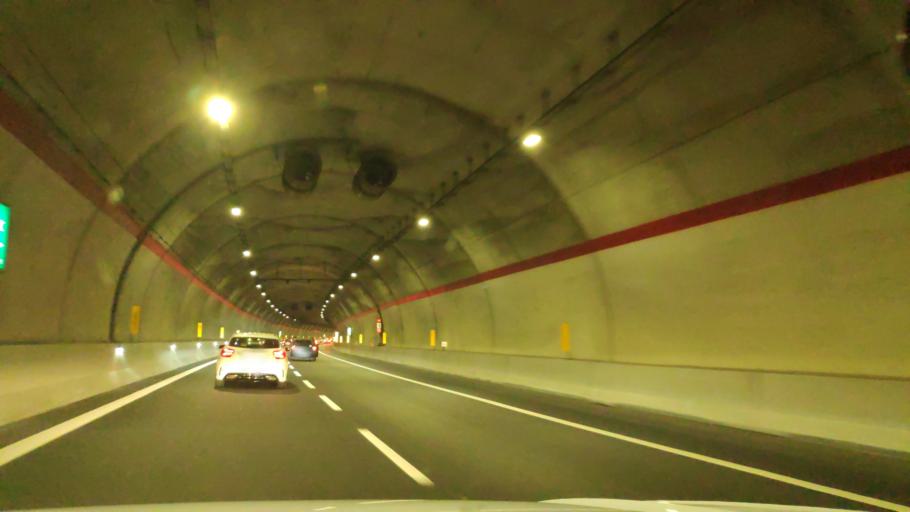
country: IT
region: Calabria
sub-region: Provincia di Cosenza
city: Mormanno
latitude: 39.8841
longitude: 15.9843
